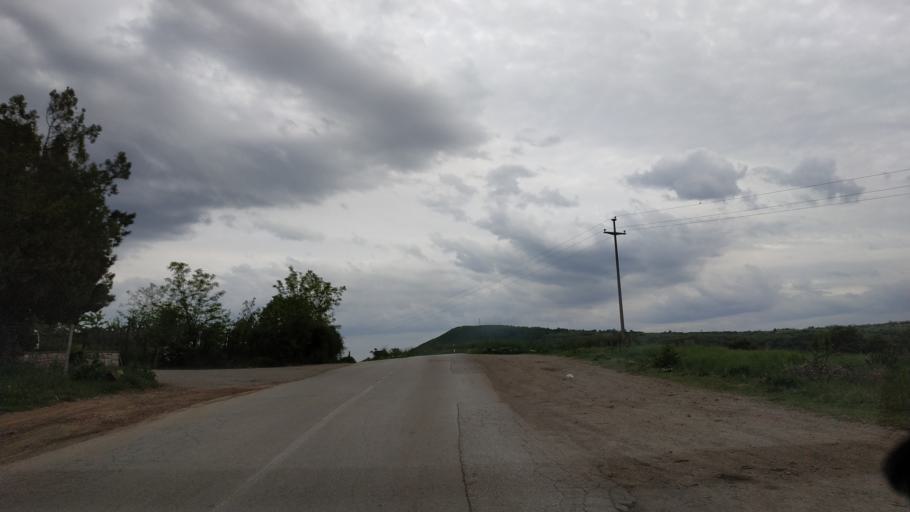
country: RS
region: Central Serbia
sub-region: Nisavski Okrug
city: Aleksinac
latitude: 43.6000
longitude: 21.6869
